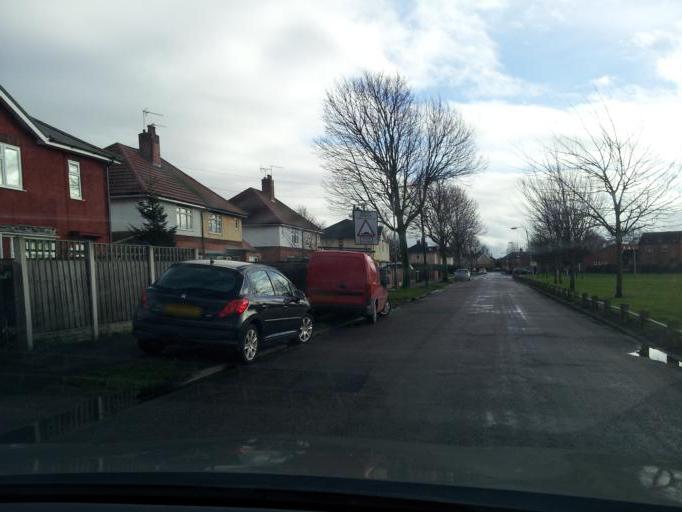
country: GB
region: England
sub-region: Nottinghamshire
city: Newark on Trent
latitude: 53.0659
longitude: -0.8099
